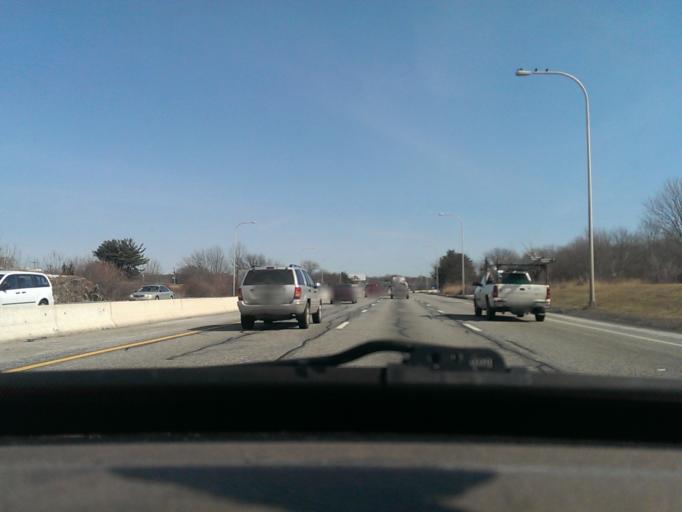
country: US
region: Massachusetts
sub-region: Bristol County
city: Seekonk
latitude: 41.8108
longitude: -71.3513
